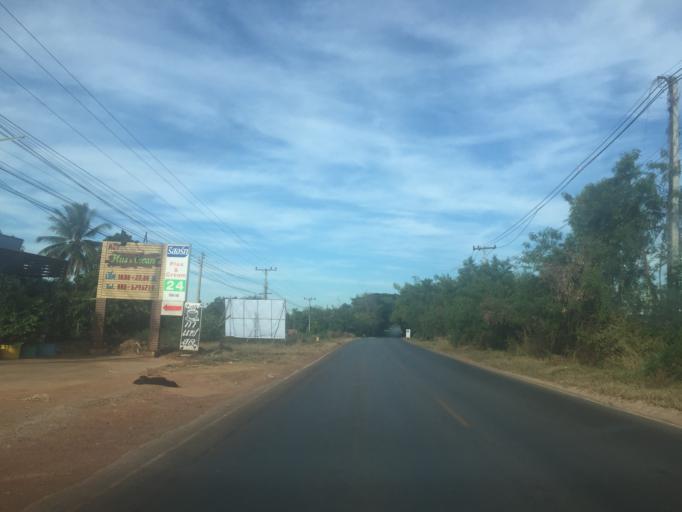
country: TH
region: Changwat Udon Thani
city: Si That
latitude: 16.9768
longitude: 103.1955
